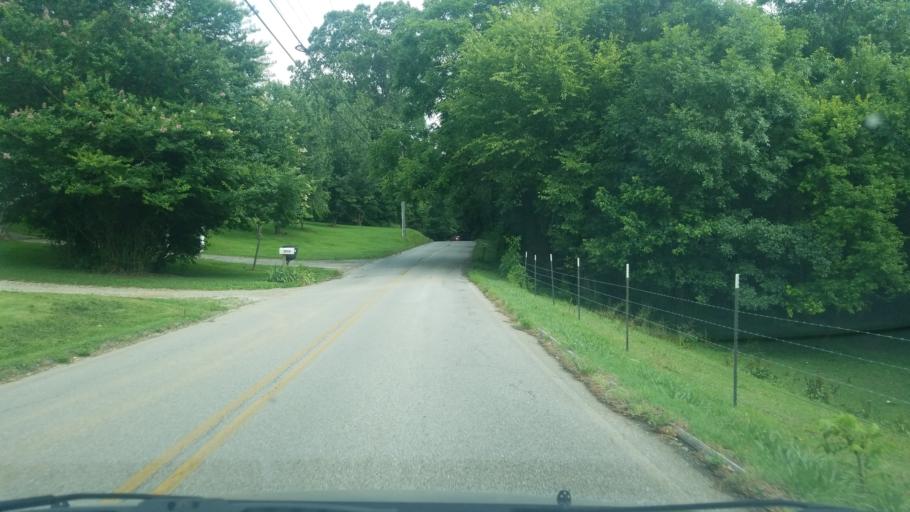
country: US
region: Tennessee
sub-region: Hamilton County
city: Apison
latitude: 35.0249
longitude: -85.0464
